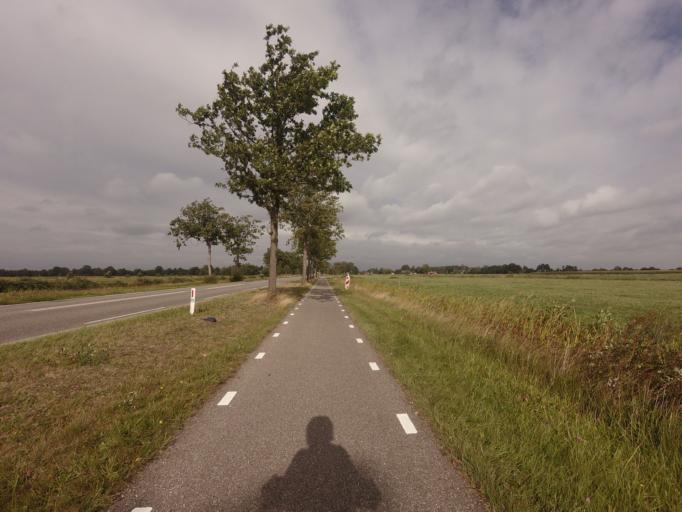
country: NL
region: Friesland
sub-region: Gemeente Opsterland
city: Gorredijk
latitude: 52.9916
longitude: 6.0839
